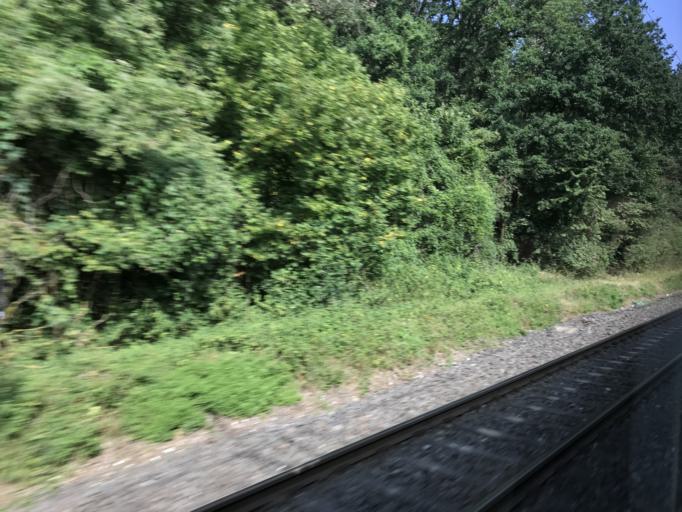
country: DE
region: Hesse
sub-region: Regierungsbezirk Giessen
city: Runkel
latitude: 50.3828
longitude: 8.1328
